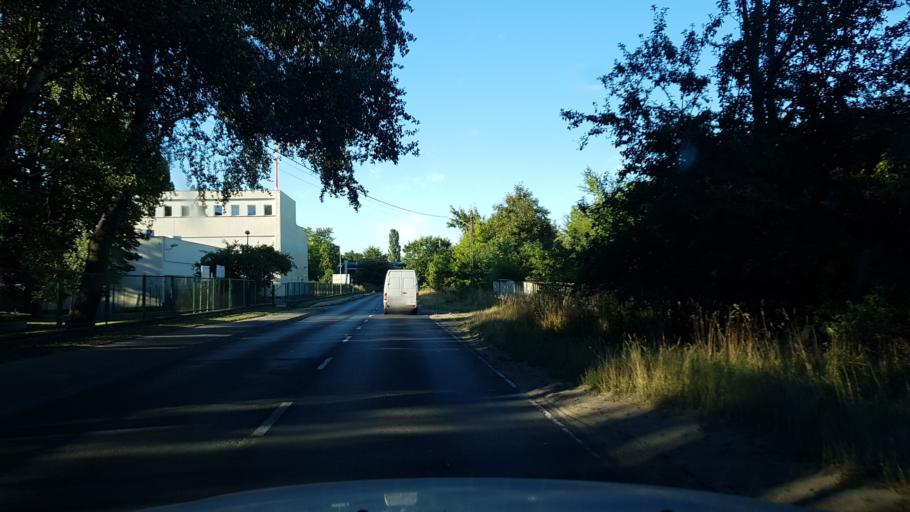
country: PL
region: West Pomeranian Voivodeship
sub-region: Szczecin
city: Szczecin
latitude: 53.3932
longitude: 14.5291
